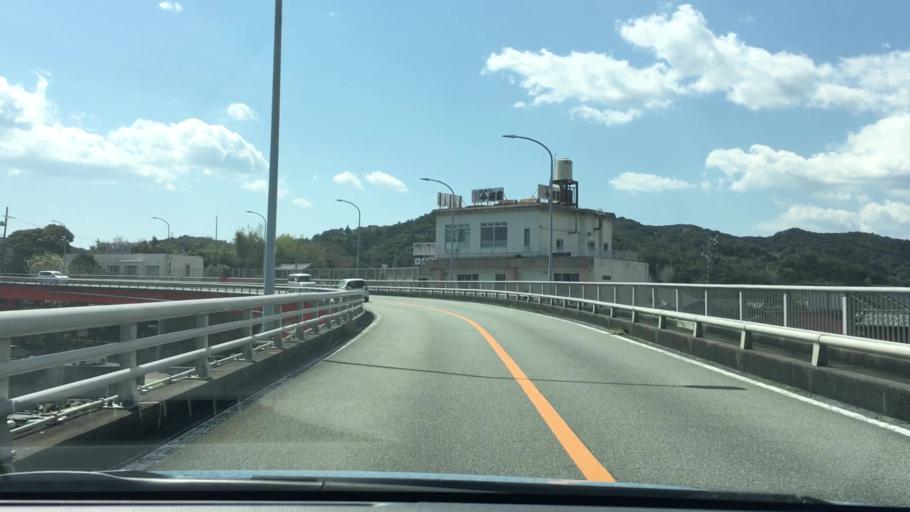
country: JP
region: Mie
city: Toba
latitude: 34.4421
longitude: 136.8803
